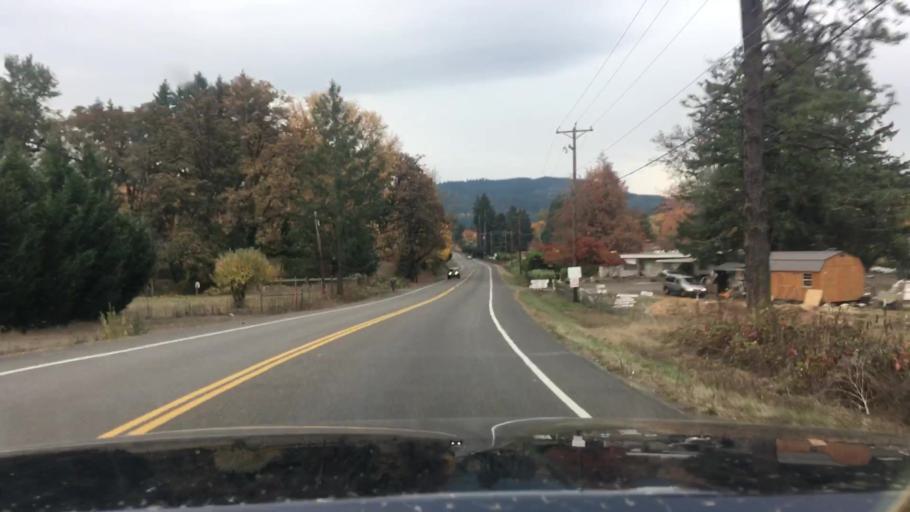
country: US
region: Oregon
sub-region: Lane County
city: Cottage Grove
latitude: 43.7690
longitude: -123.0624
